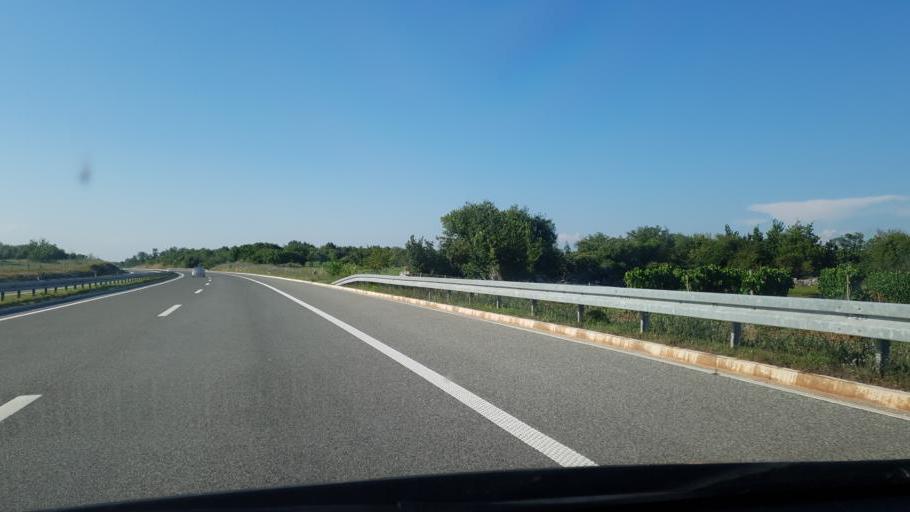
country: HR
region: Istarska
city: Vodnjan
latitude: 44.9672
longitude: 13.8727
